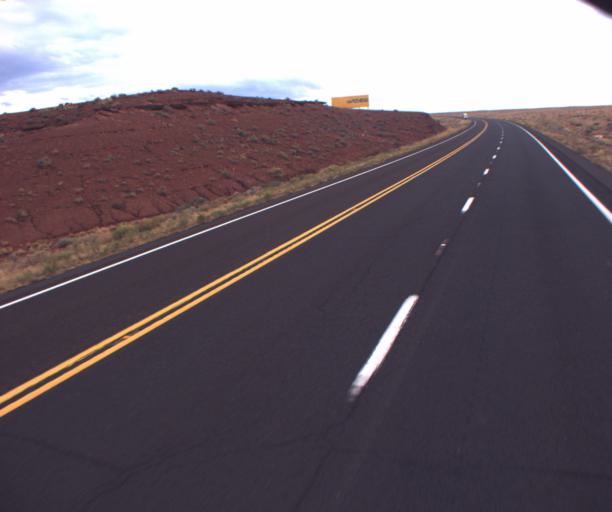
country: US
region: Arizona
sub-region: Coconino County
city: Tuba City
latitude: 35.7768
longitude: -111.4604
